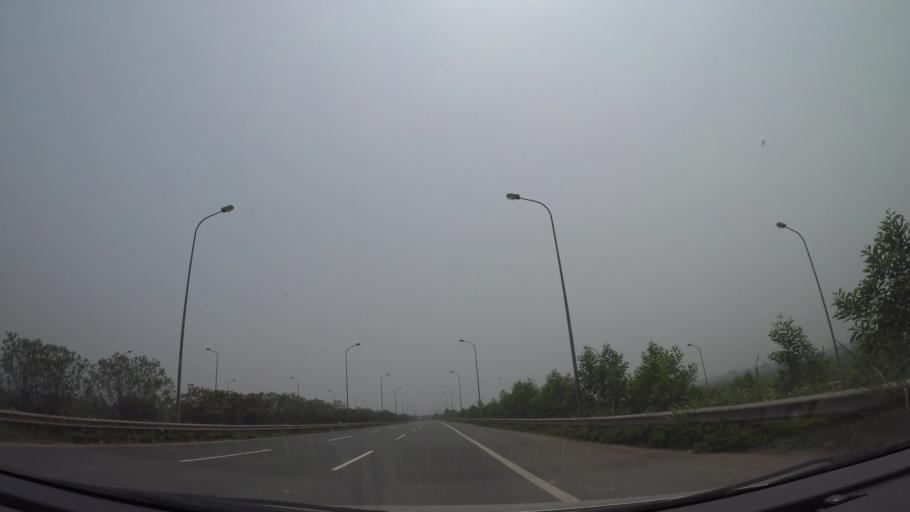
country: VN
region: Ha Noi
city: Quoc Oai
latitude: 21.0013
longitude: 105.6175
